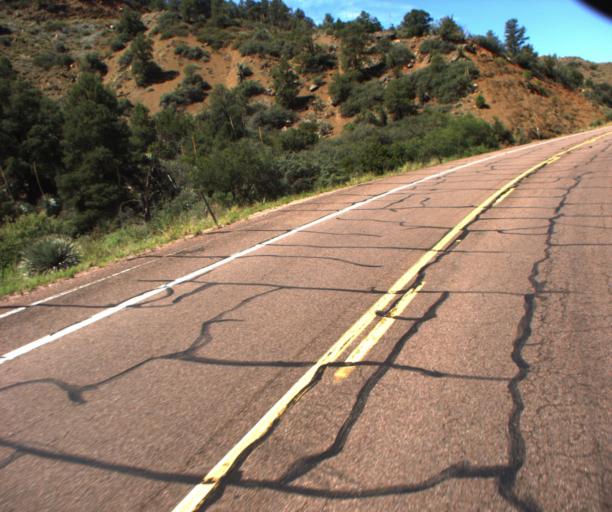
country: US
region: Arizona
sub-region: Navajo County
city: Cibecue
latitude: 33.7954
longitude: -110.5014
